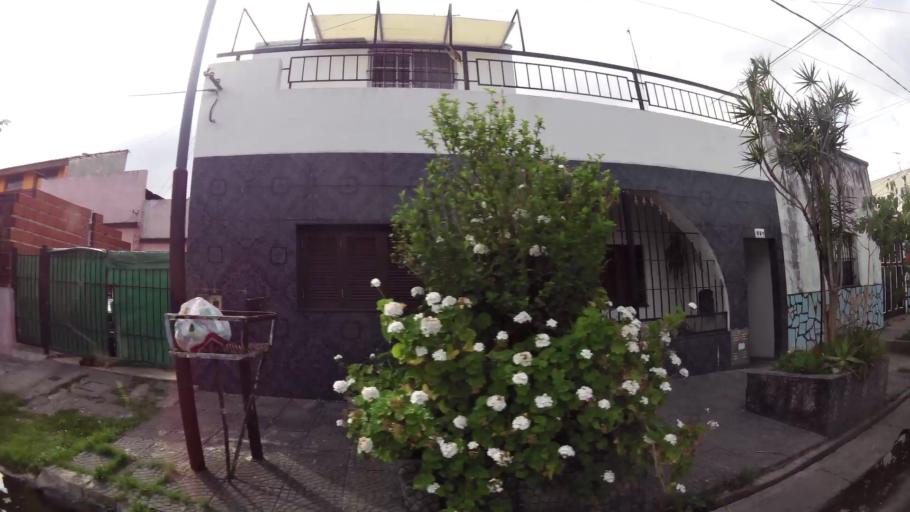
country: AR
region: Buenos Aires
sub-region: Partido de Lanus
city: Lanus
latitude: -34.6935
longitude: -58.3804
